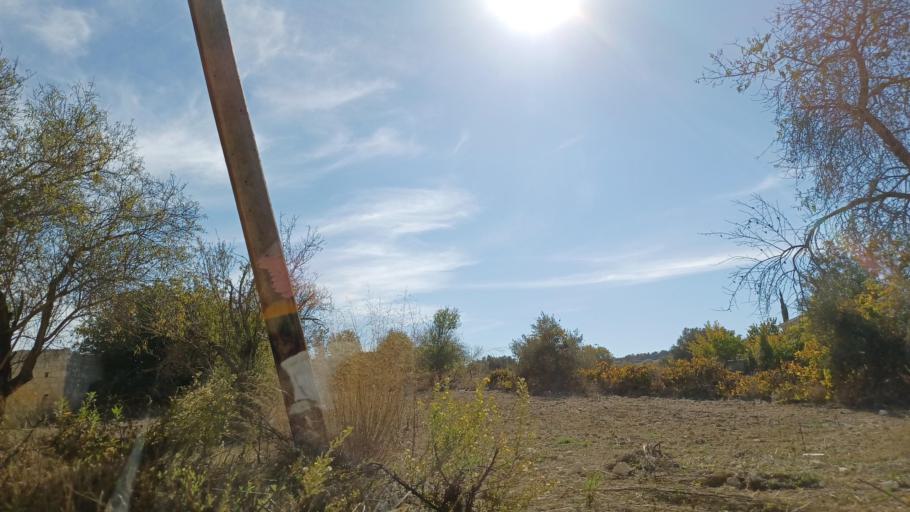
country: CY
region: Pafos
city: Pegeia
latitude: 34.9424
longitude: 32.4468
